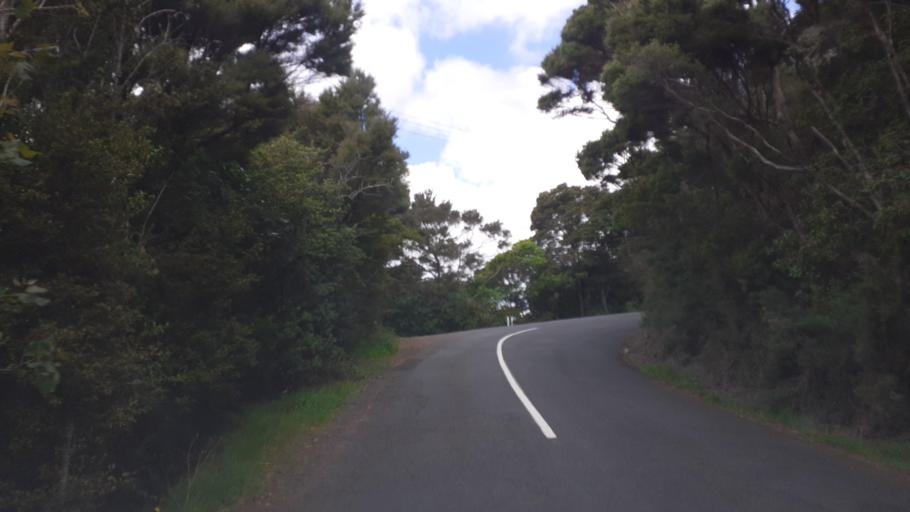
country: NZ
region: Northland
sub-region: Far North District
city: Paihia
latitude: -35.3108
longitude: 174.1139
